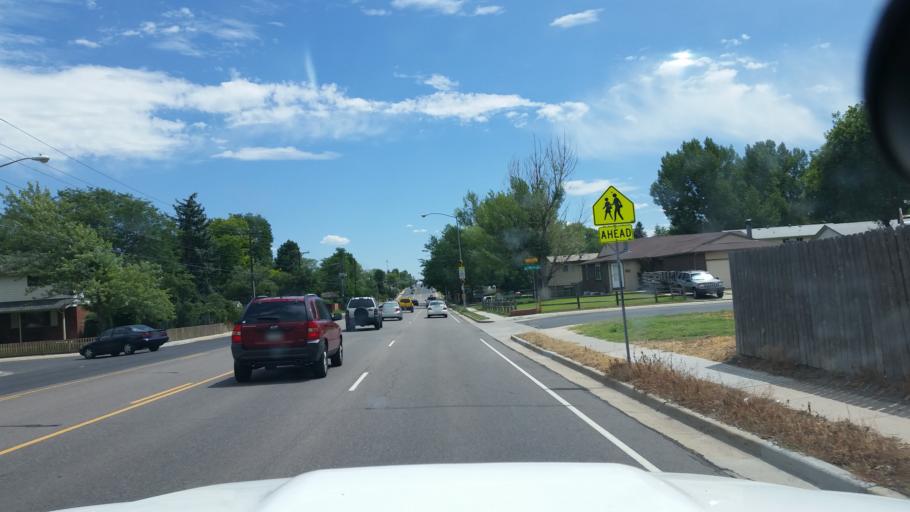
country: US
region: Colorado
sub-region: Adams County
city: Westminster
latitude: 39.8634
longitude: -105.0388
